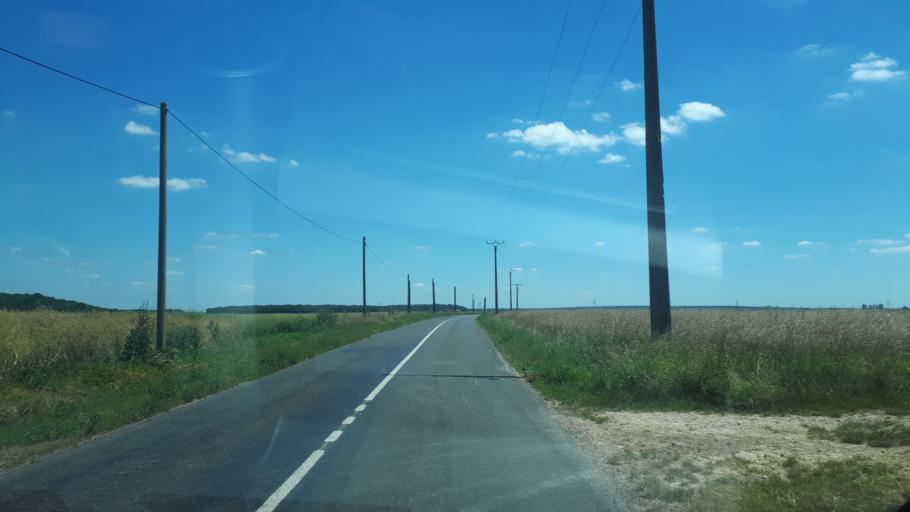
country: FR
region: Centre
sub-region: Departement du Loir-et-Cher
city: Herbault
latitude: 47.6484
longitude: 1.1873
